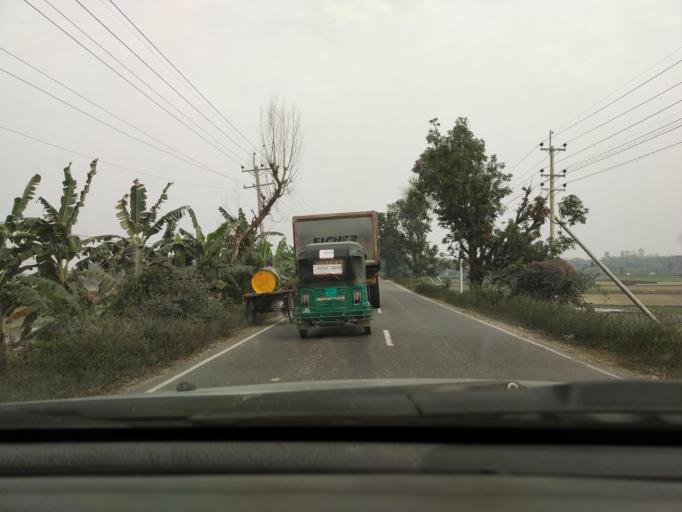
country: BD
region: Dhaka
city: Narsingdi
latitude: 24.0177
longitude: 90.7375
